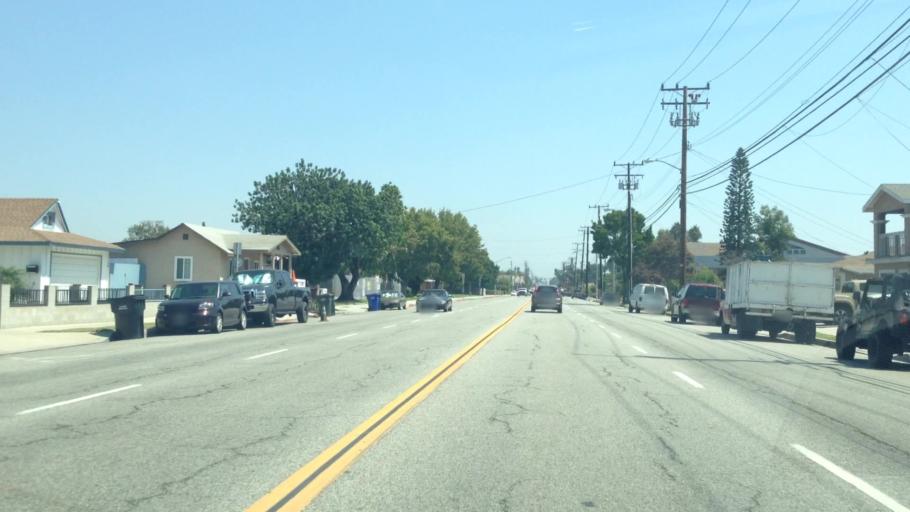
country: US
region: California
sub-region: Los Angeles County
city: West Carson
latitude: 33.8245
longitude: -118.2976
